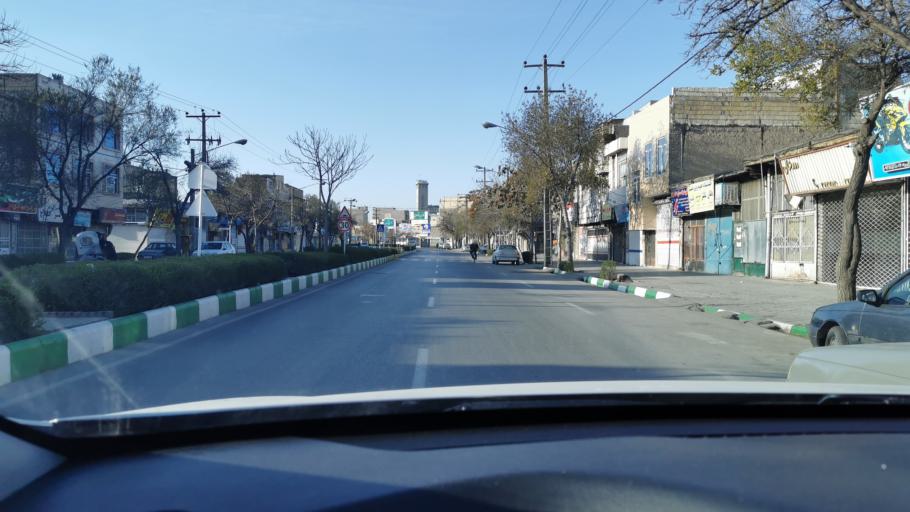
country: IR
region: Razavi Khorasan
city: Mashhad
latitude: 36.3080
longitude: 59.6349
